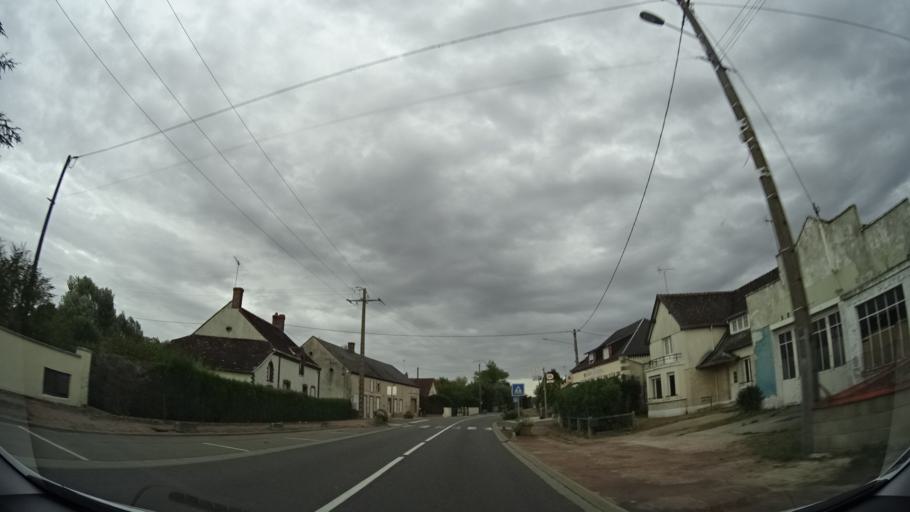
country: FR
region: Centre
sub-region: Departement du Loiret
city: Amilly
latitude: 47.9588
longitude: 2.8024
